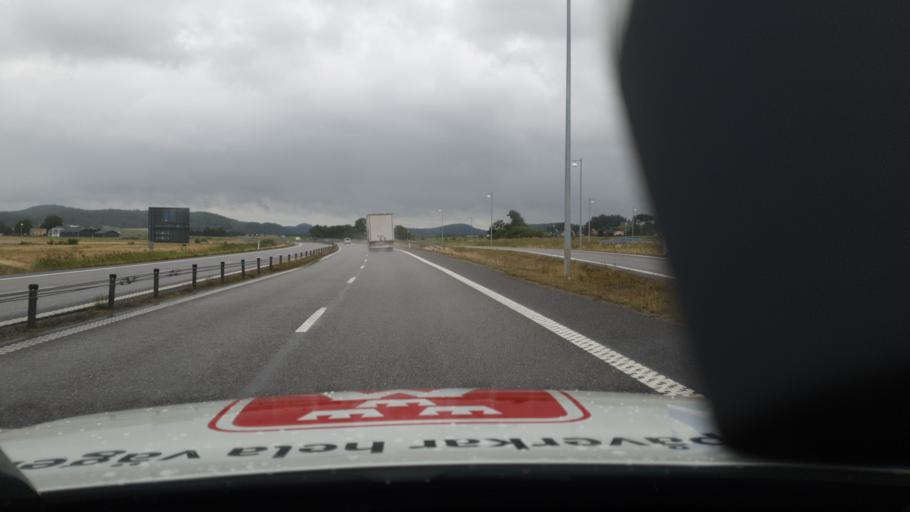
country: SE
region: Vaestra Goetaland
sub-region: Ale Kommun
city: Alvangen
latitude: 57.9672
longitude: 12.1445
